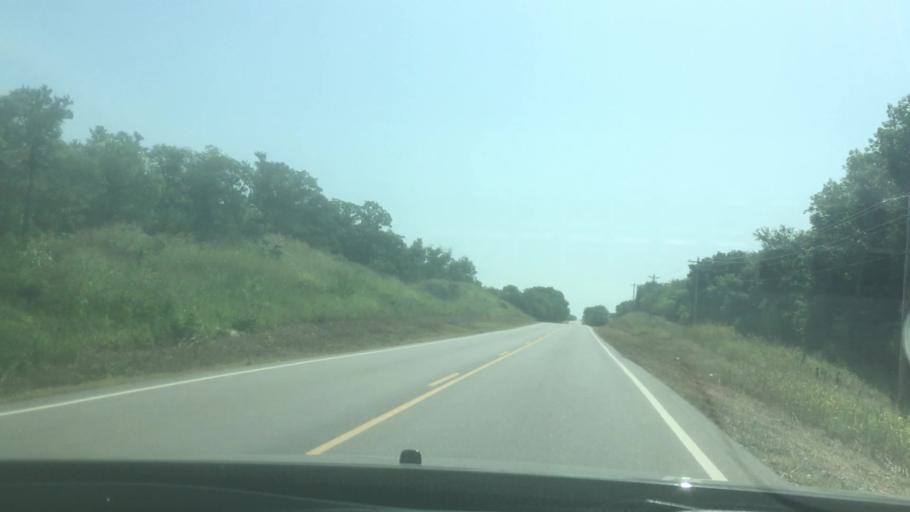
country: US
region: Oklahoma
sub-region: Bryan County
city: Durant
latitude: 34.1427
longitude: -96.3946
